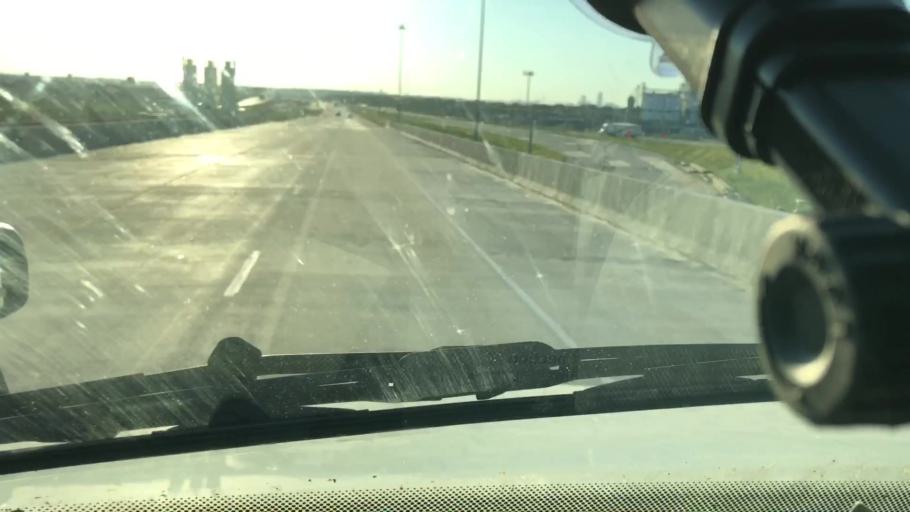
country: US
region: Iowa
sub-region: Pottawattamie County
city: Council Bluffs
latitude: 41.2323
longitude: -95.8409
